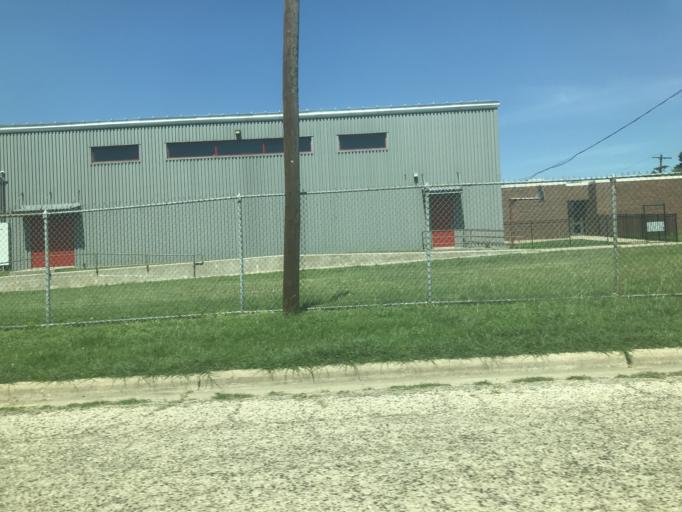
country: US
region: Texas
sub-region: Taylor County
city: Abilene
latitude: 32.4694
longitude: -99.7361
